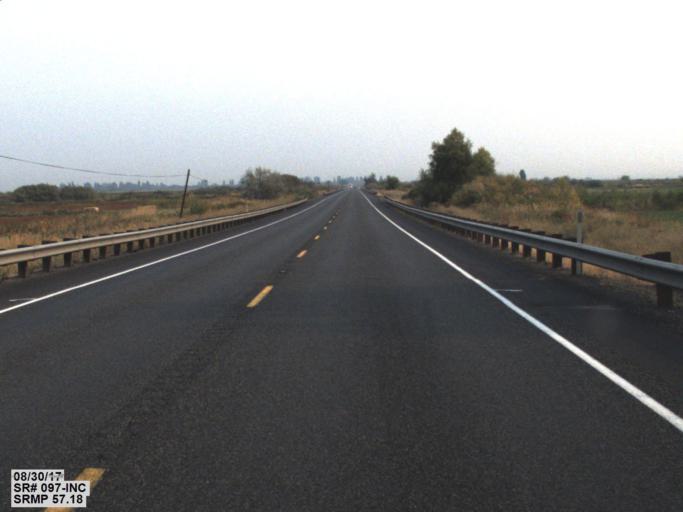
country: US
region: Washington
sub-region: Yakima County
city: Toppenish
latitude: 46.3107
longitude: -120.3306
